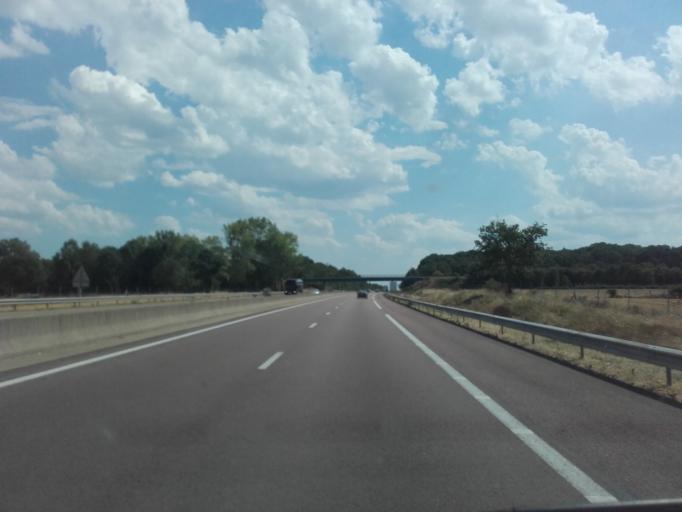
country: FR
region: Bourgogne
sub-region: Departement de l'Yonne
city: Avallon
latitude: 47.5267
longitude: 3.9854
